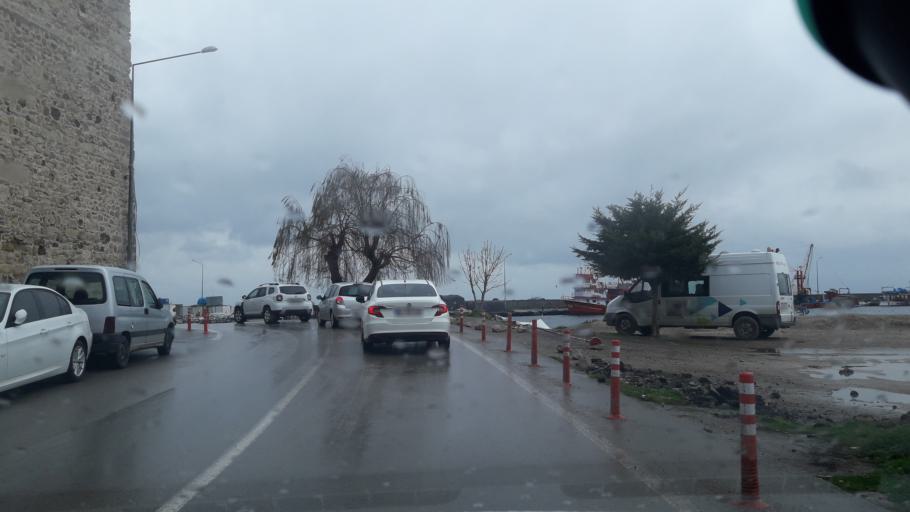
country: TR
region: Sinop
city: Sinop
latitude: 42.0243
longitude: 35.1461
